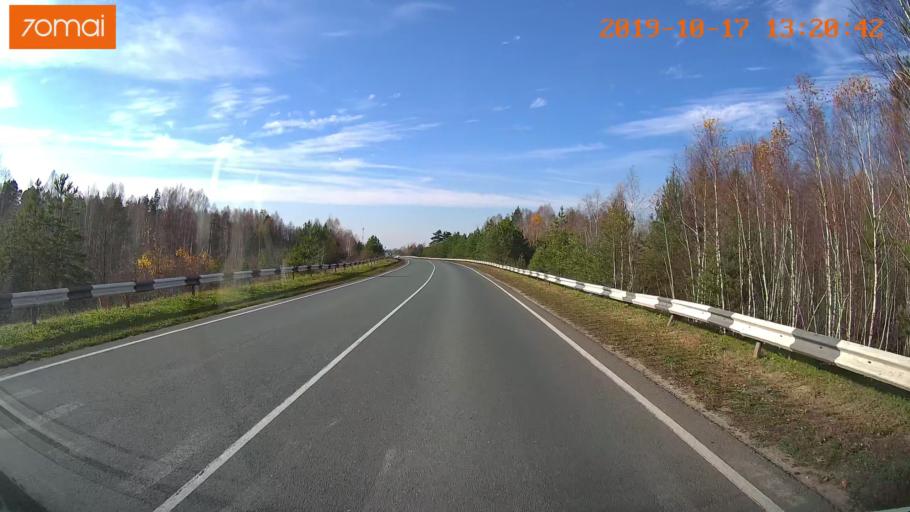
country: RU
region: Rjazan
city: Gus'-Zheleznyy
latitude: 55.0780
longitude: 41.0453
